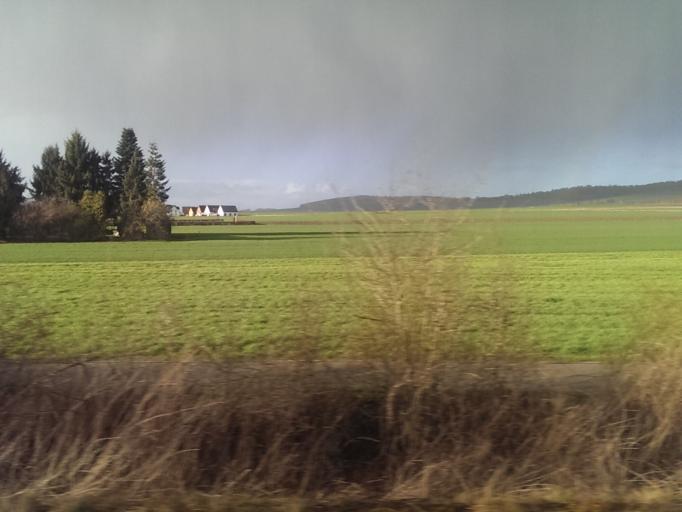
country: DE
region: Lower Saxony
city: Giesen
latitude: 52.1601
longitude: 9.8779
